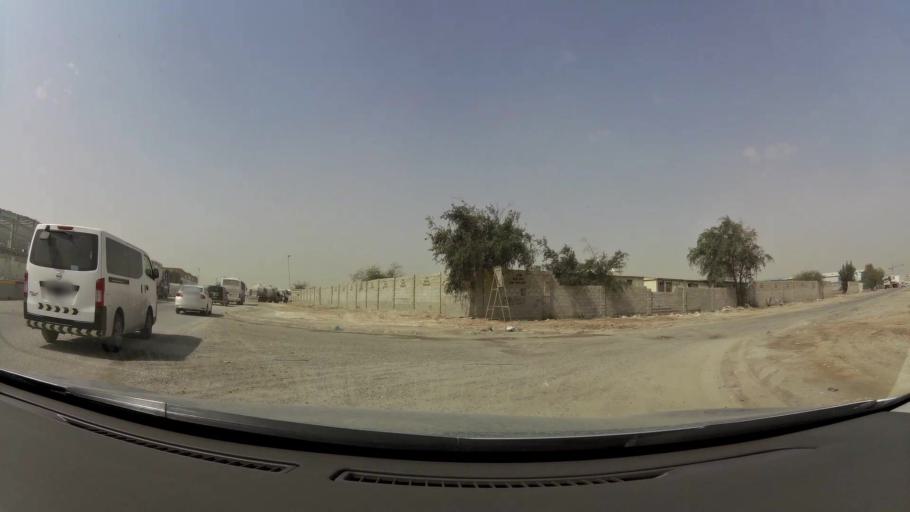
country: QA
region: Al Wakrah
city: Al Wukayr
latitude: 25.1650
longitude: 51.4427
